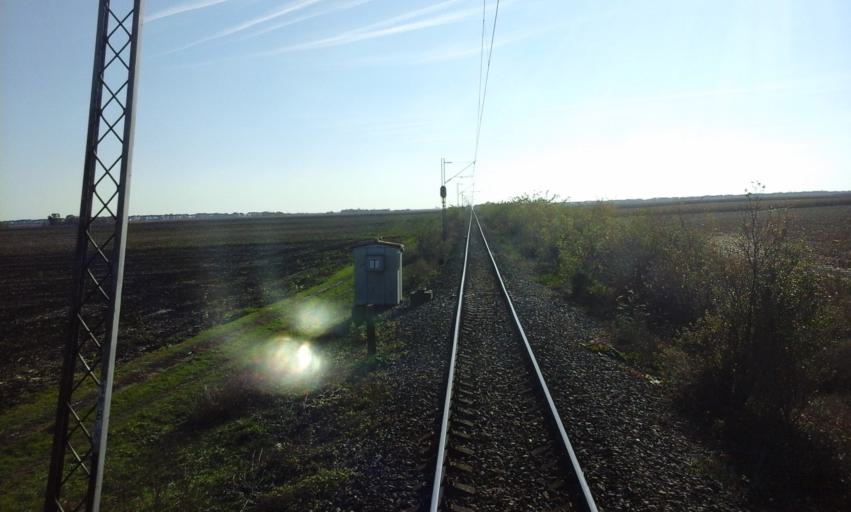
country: RS
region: Autonomna Pokrajina Vojvodina
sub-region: Severnobacki Okrug
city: Backa Topola
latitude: 45.9011
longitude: 19.6623
